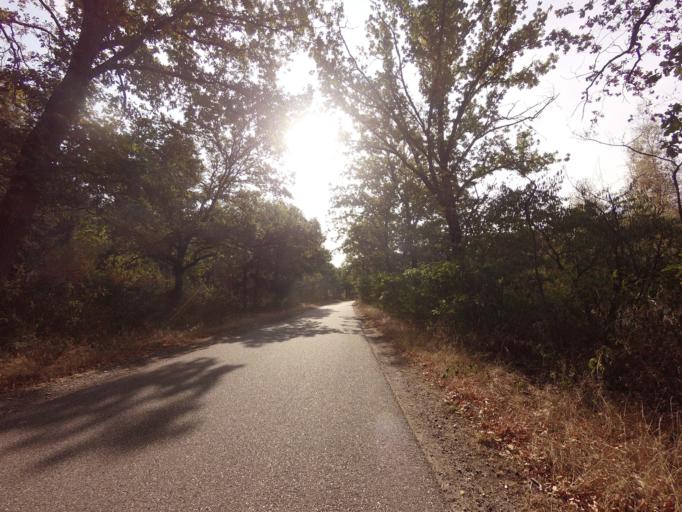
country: NL
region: North Brabant
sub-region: Gemeente Mill en Sint Hubert
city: Wilbertoord
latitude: 51.6621
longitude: 5.7791
